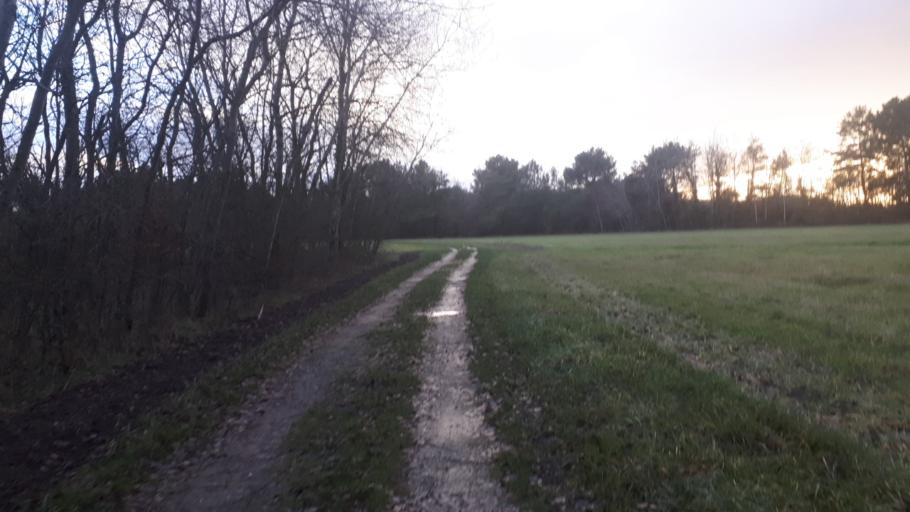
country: FR
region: Centre
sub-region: Departement du Loir-et-Cher
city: Saint-Romain-sur-Cher
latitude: 47.3470
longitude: 1.3956
